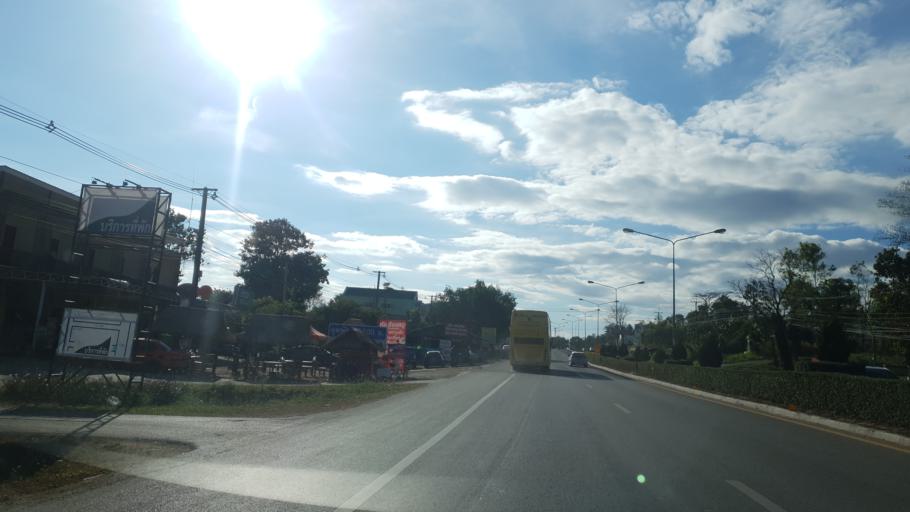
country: TH
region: Loei
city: Phu Ruea
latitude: 17.4574
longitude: 101.3715
